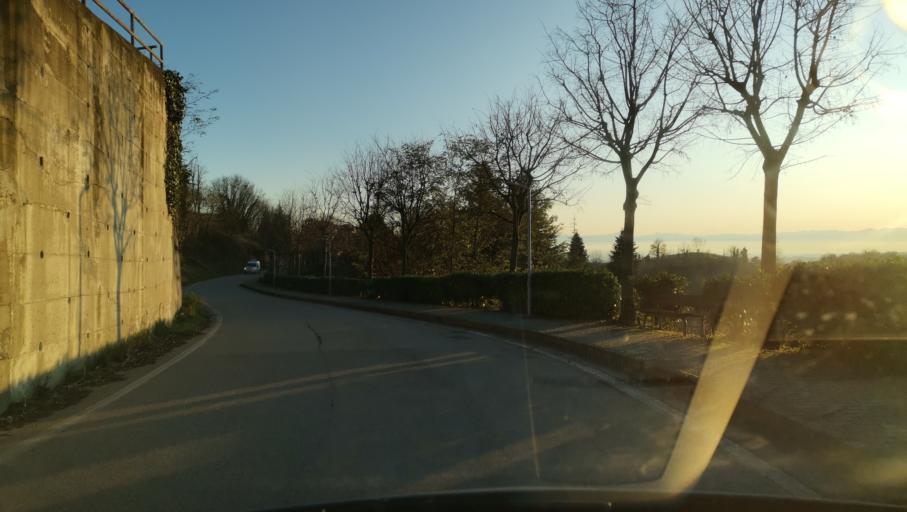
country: IT
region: Piedmont
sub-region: Provincia di Torino
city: Cinzano
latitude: 45.0922
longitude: 7.9236
